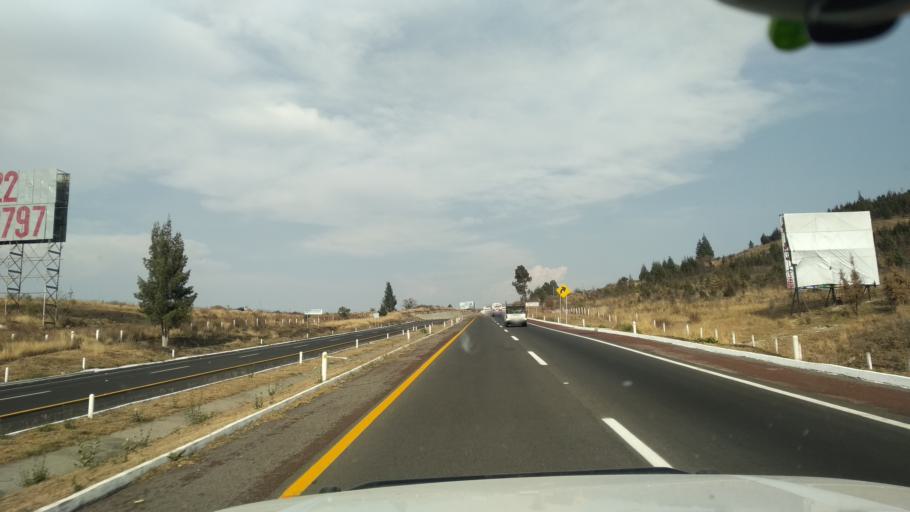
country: MX
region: Puebla
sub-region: Santa Isabel Cholula
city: San Pablo Ahuatempa
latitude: 18.9765
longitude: -98.3623
